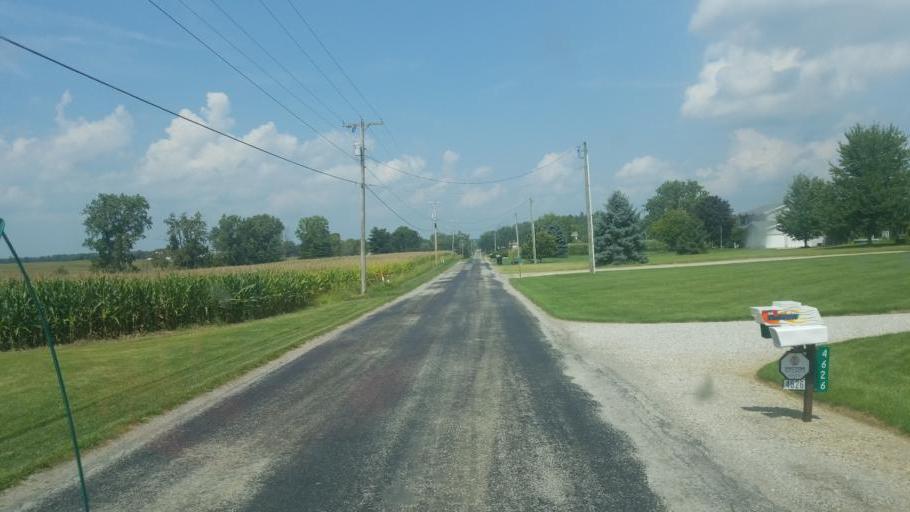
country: US
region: Ohio
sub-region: Richland County
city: Shelby
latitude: 40.8798
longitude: -82.5956
